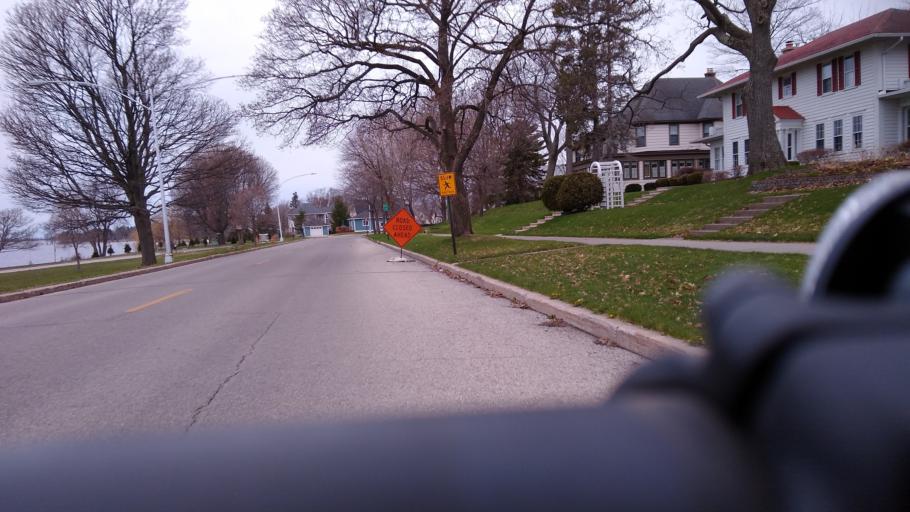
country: US
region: Michigan
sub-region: Delta County
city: Escanaba
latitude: 45.7382
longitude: -87.0572
